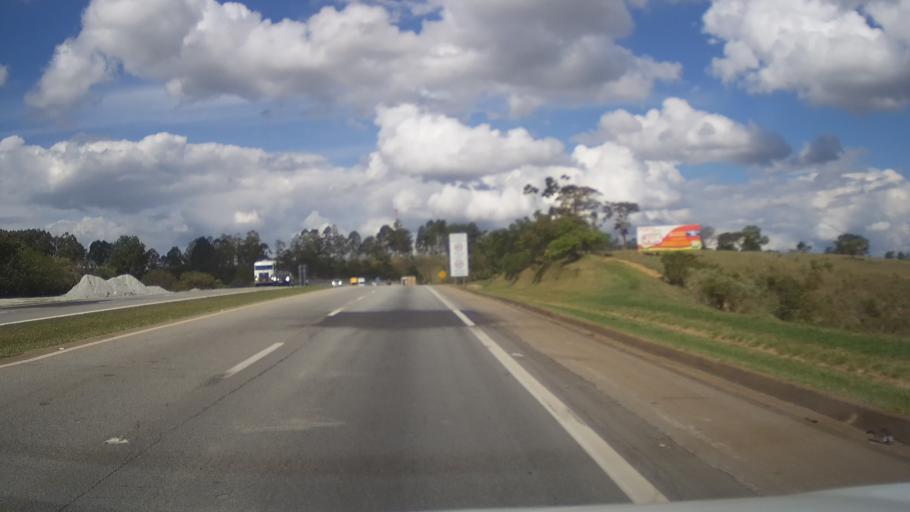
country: BR
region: Minas Gerais
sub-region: Oliveira
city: Oliveira
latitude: -20.8270
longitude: -44.8048
